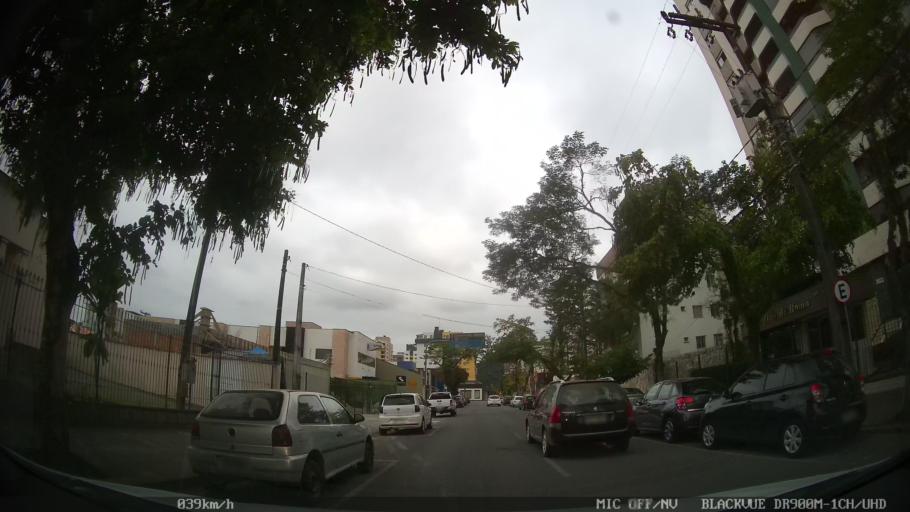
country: BR
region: Santa Catarina
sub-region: Joinville
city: Joinville
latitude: -26.2959
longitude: -48.8490
